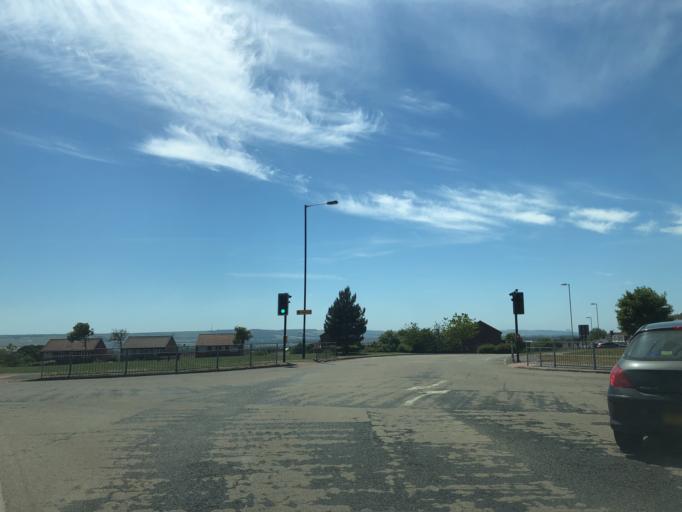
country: GB
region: England
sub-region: North Yorkshire
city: Scarborough
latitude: 54.2452
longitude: -0.3849
